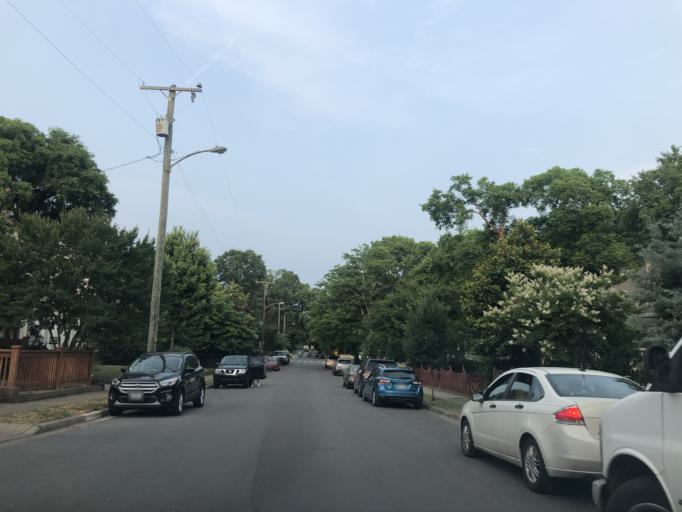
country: US
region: Tennessee
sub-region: Davidson County
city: Oak Hill
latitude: 36.1235
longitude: -86.7878
